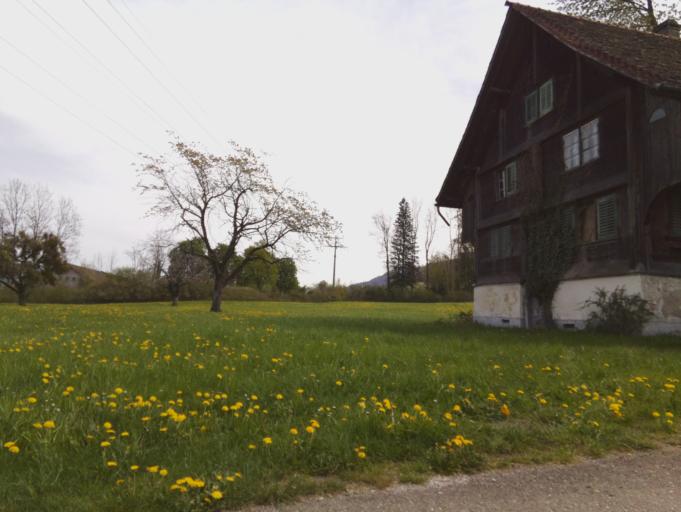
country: CH
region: Schwyz
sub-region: Bezirk March
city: Lachen
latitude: 47.1798
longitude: 8.8537
